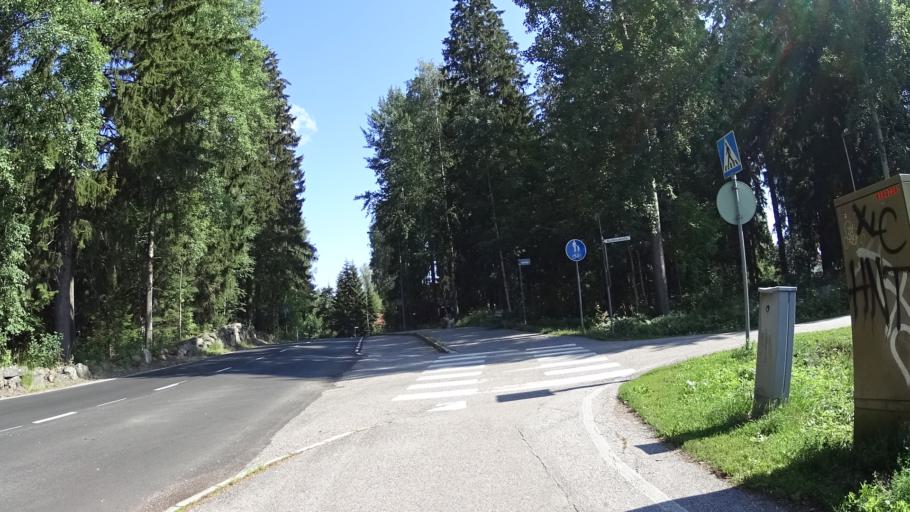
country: FI
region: Uusimaa
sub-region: Helsinki
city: Tuusula
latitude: 60.4085
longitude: 25.0290
